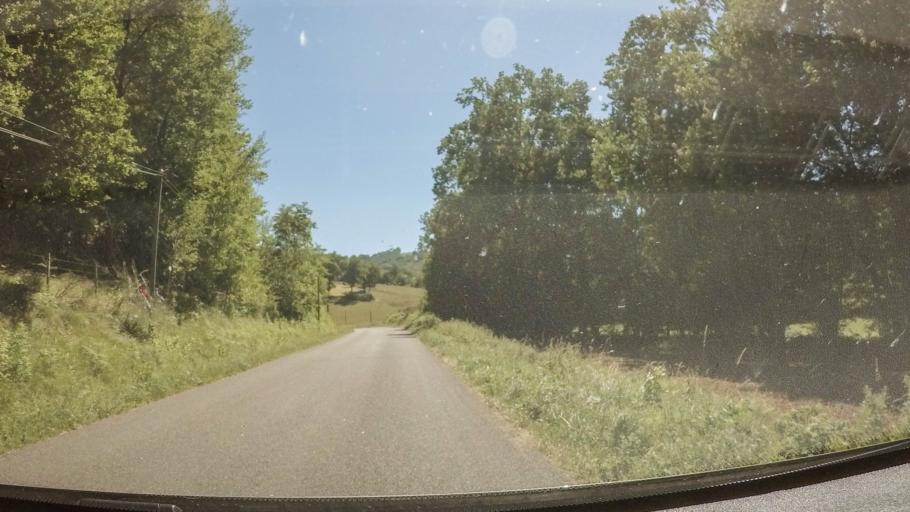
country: FR
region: Midi-Pyrenees
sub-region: Departement de l'Aveyron
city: Firmi
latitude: 44.4801
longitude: 2.3416
